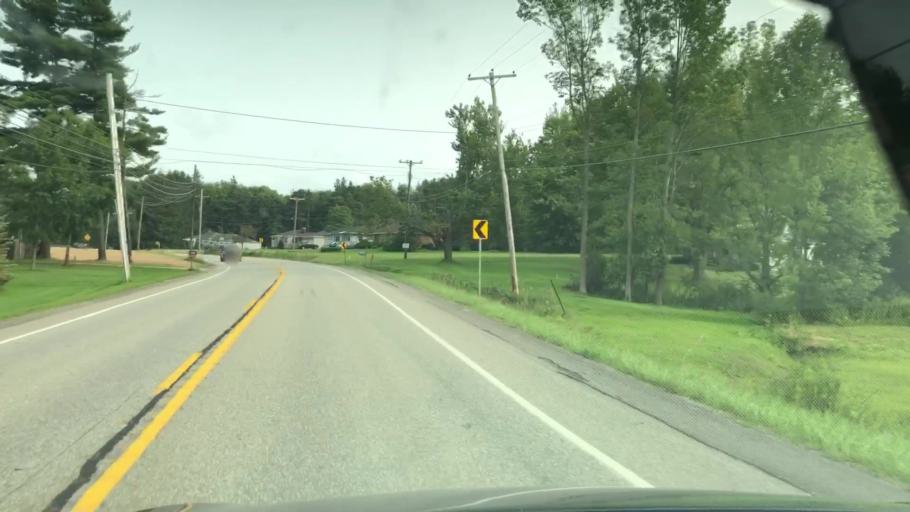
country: US
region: Pennsylvania
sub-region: Erie County
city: Wesleyville
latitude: 42.0690
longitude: -79.9818
